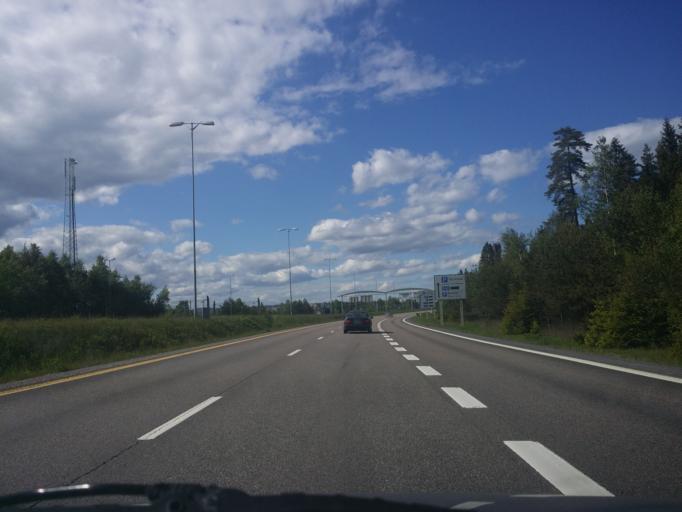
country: NO
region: Akershus
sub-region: Nannestad
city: Teigebyen
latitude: 60.1789
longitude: 11.0944
